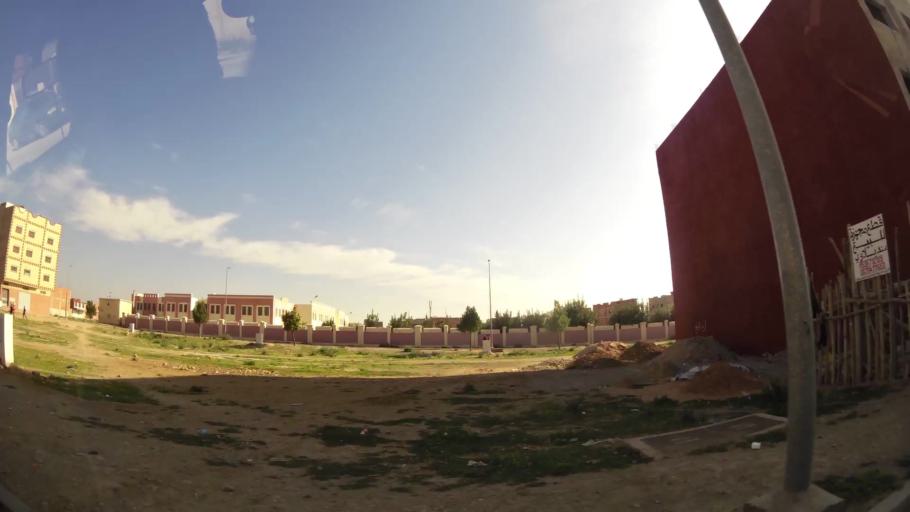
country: MA
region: Oriental
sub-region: Oujda-Angad
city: Oujda
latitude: 34.7117
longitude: -1.8951
